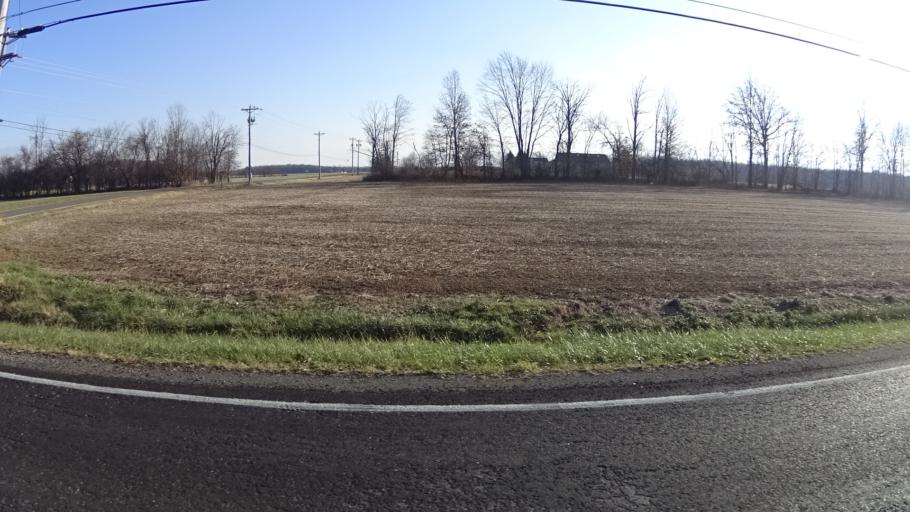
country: US
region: Ohio
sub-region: Lorain County
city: Lagrange
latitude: 41.2745
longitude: -82.1573
